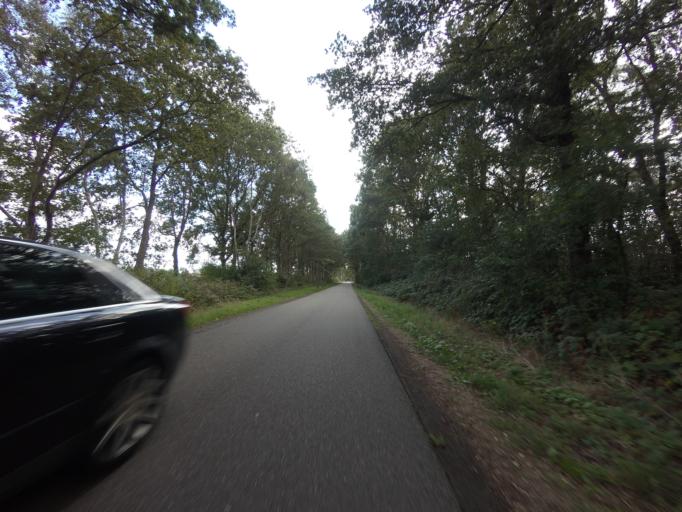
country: NL
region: Friesland
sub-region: Gemeente Heerenveen
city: Jubbega
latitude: 52.9919
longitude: 6.2288
